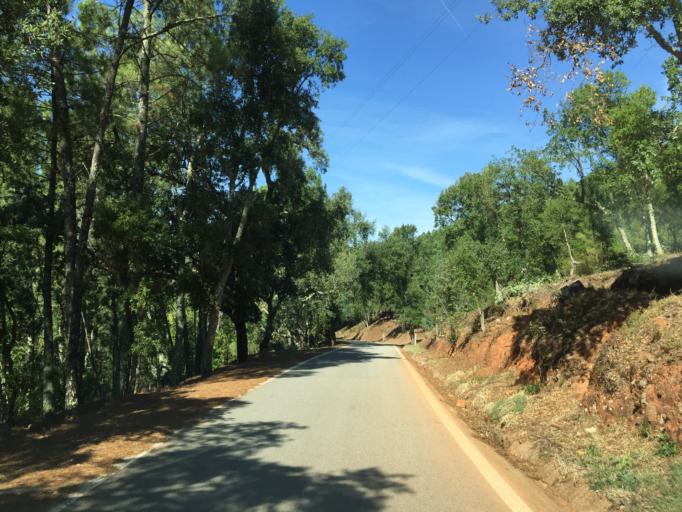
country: PT
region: Portalegre
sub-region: Marvao
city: Marvao
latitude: 39.3755
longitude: -7.3837
